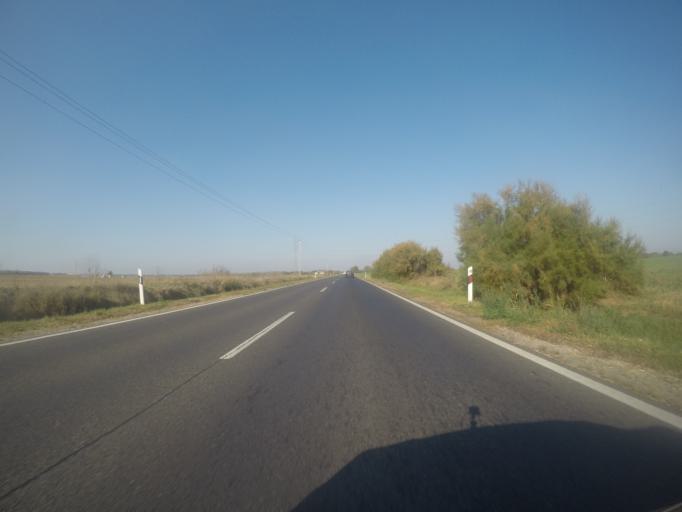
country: HU
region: Fejer
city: Baracs
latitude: 46.8443
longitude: 18.9112
